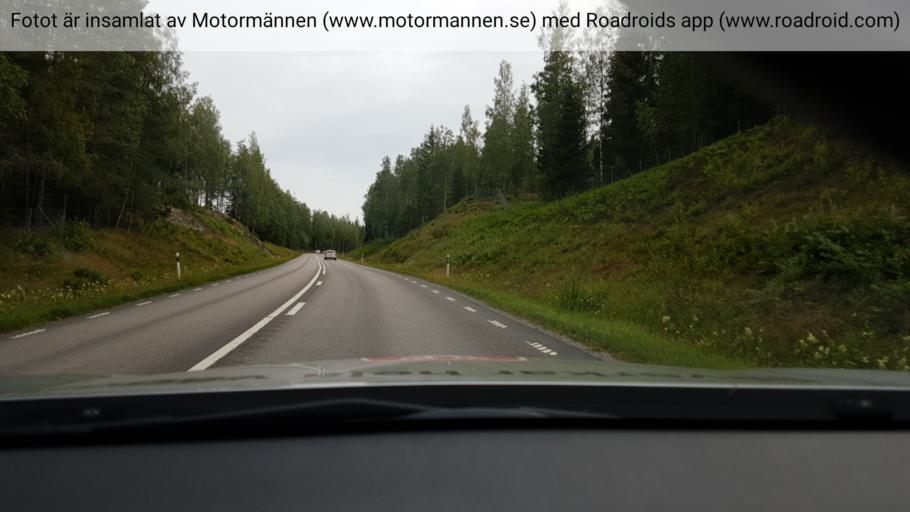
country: SE
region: Vaestra Goetaland
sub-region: Bengtsfors Kommun
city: Billingsfors
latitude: 59.0037
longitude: 12.2687
